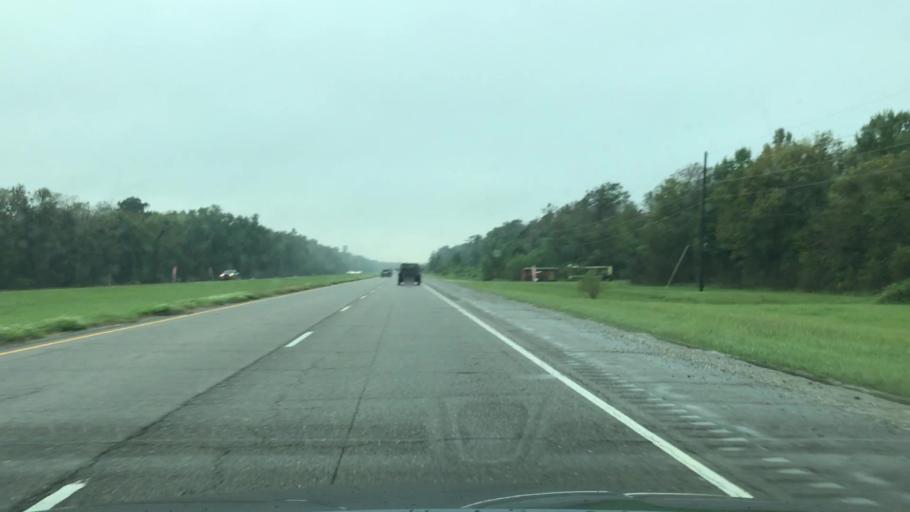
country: US
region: Louisiana
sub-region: Lafourche Parish
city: Raceland
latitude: 29.7369
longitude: -90.5578
